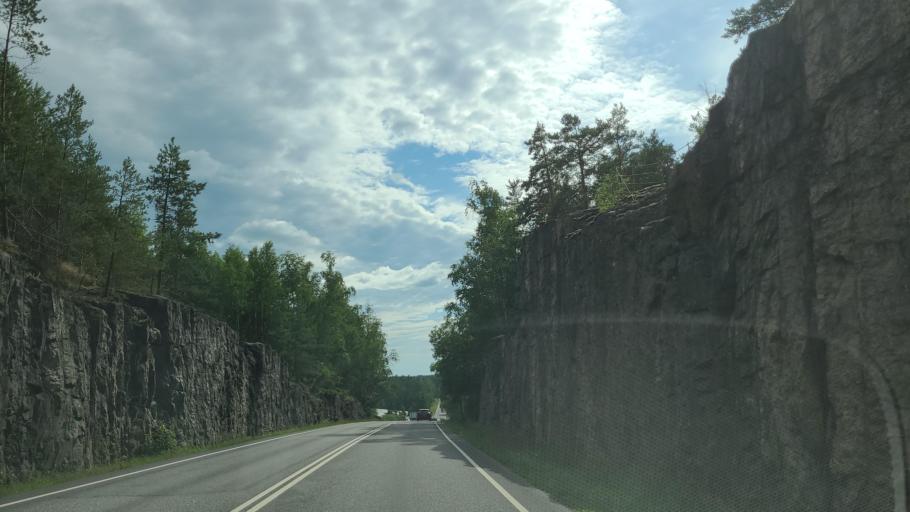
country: FI
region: Varsinais-Suomi
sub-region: Turku
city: Merimasku
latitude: 60.4546
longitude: 21.9078
